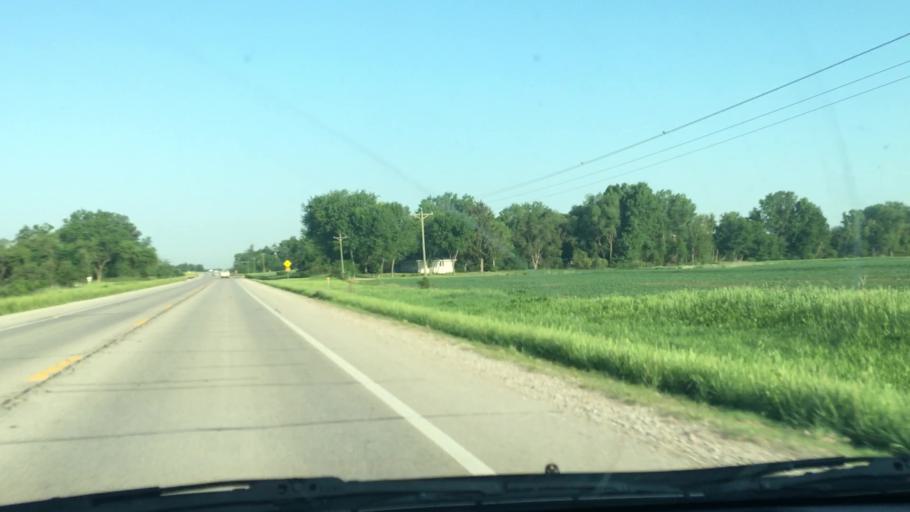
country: US
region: Iowa
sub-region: Johnson County
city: Tiffin
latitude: 41.7140
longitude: -91.7081
